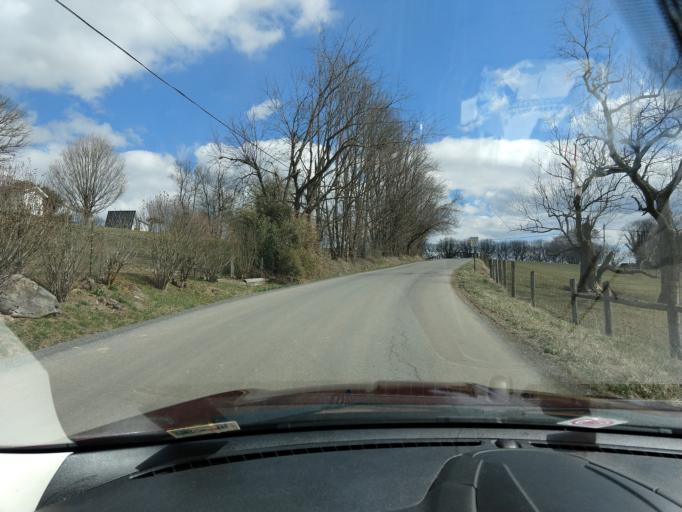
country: US
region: West Virginia
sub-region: Greenbrier County
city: Lewisburg
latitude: 37.8123
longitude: -80.4823
